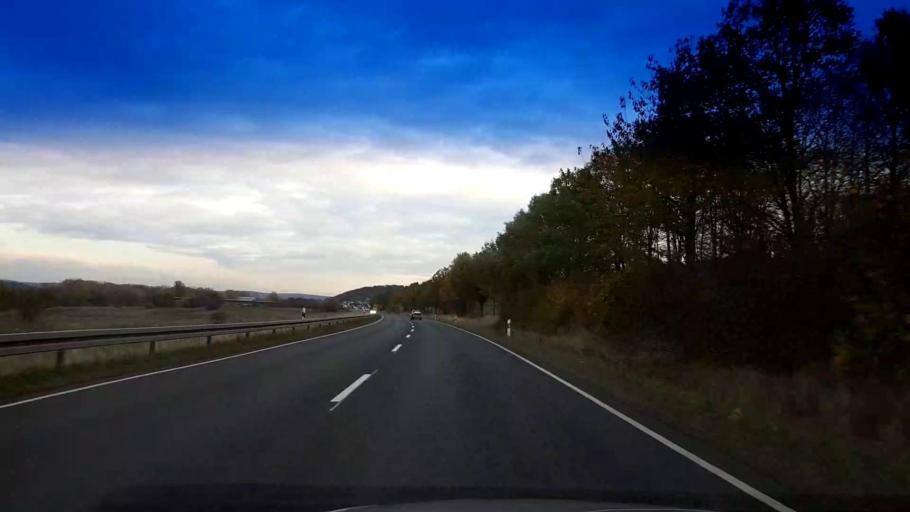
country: DE
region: Bavaria
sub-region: Upper Franconia
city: Viereth-Trunstadt
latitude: 49.9267
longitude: 10.7610
